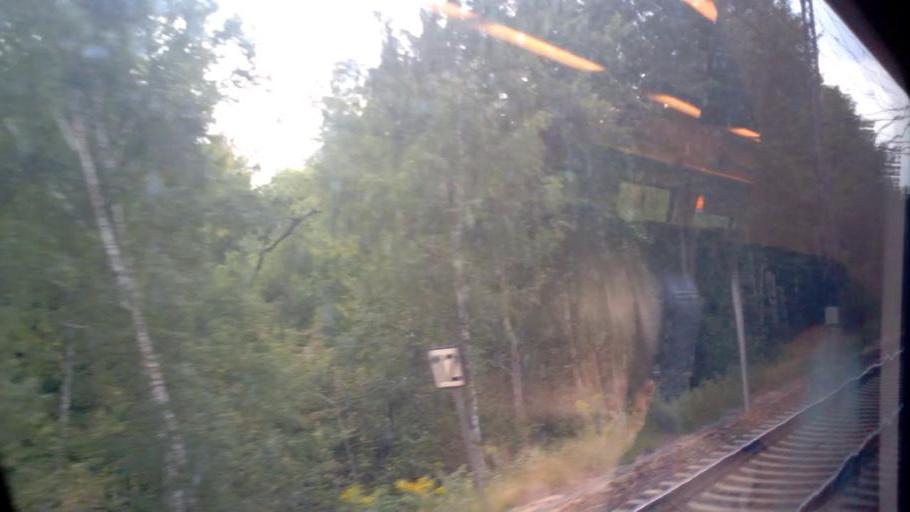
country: DE
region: Brandenburg
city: Grossbeeren
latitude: 52.3366
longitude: 13.2898
